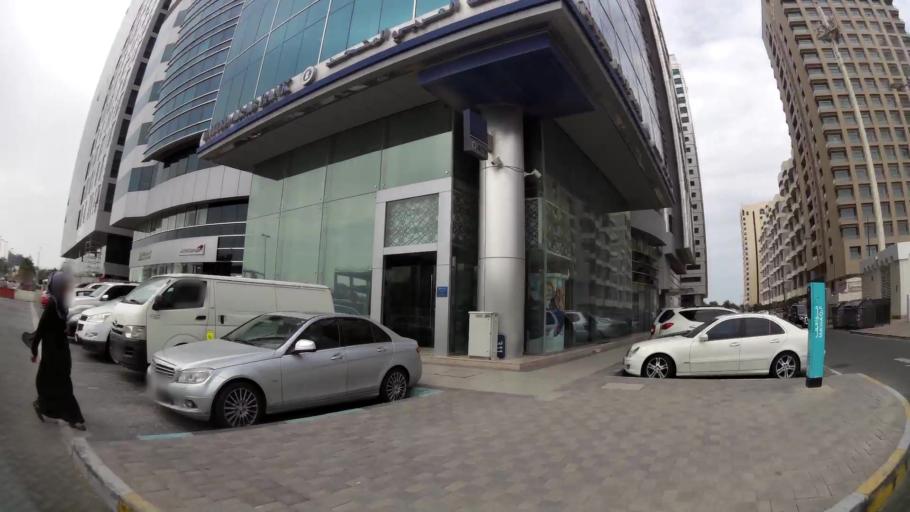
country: AE
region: Abu Dhabi
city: Abu Dhabi
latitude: 24.4683
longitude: 54.3410
